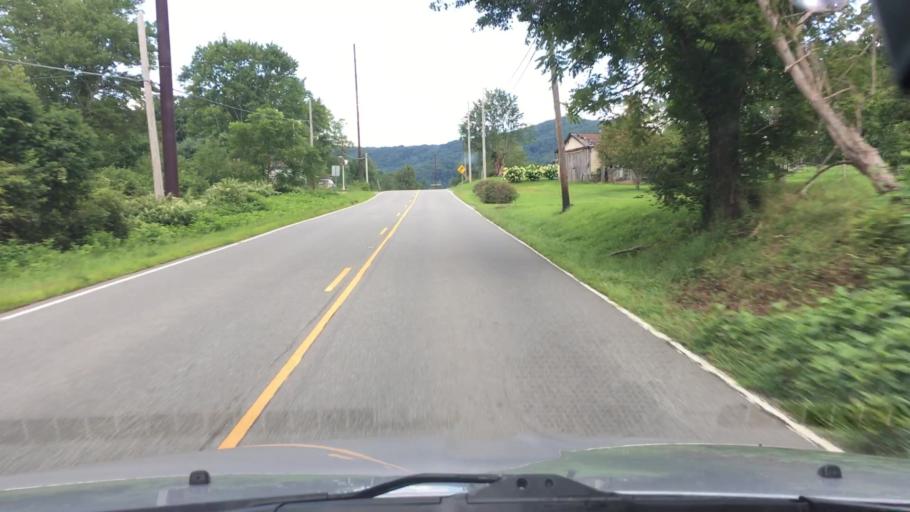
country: US
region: North Carolina
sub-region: Yancey County
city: Burnsville
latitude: 35.8482
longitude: -82.1961
